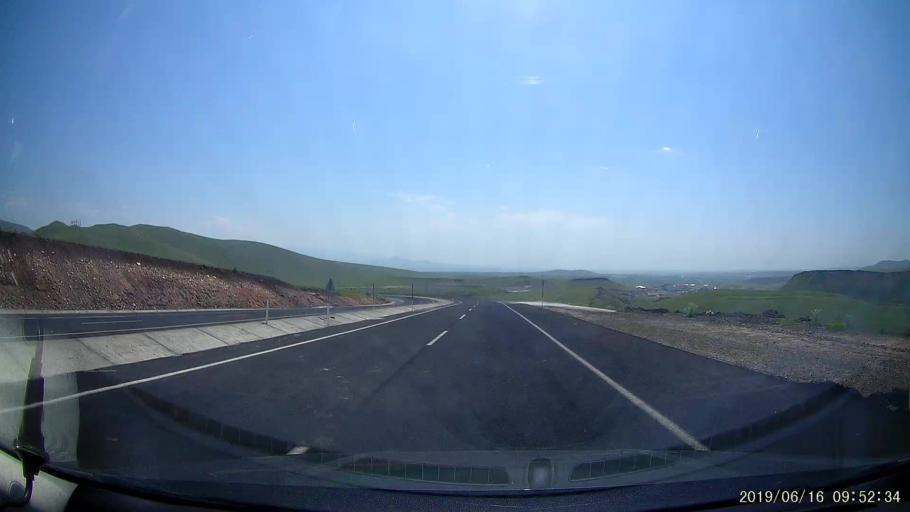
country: TR
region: Kars
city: Digor
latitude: 40.3939
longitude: 43.3896
